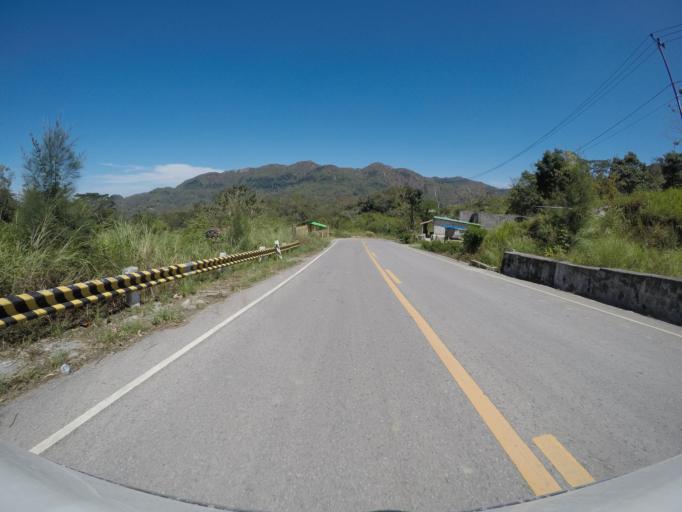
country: TL
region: Manatuto
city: Manatuto
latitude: -8.7769
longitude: 125.9667
